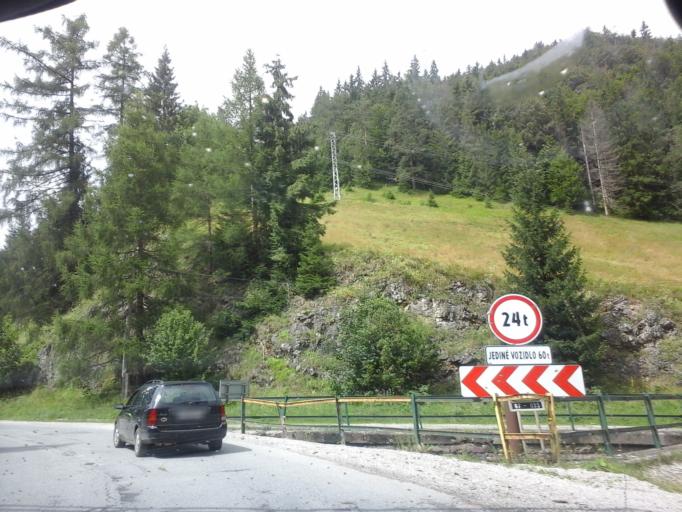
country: SK
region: Kosicky
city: Dobsina
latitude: 48.8680
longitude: 20.3476
